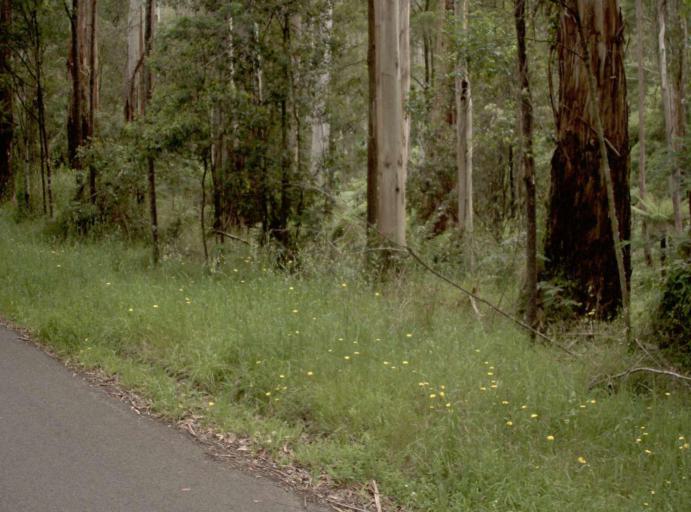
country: AU
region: Victoria
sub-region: Baw Baw
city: Warragul
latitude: -37.9163
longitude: 146.1062
